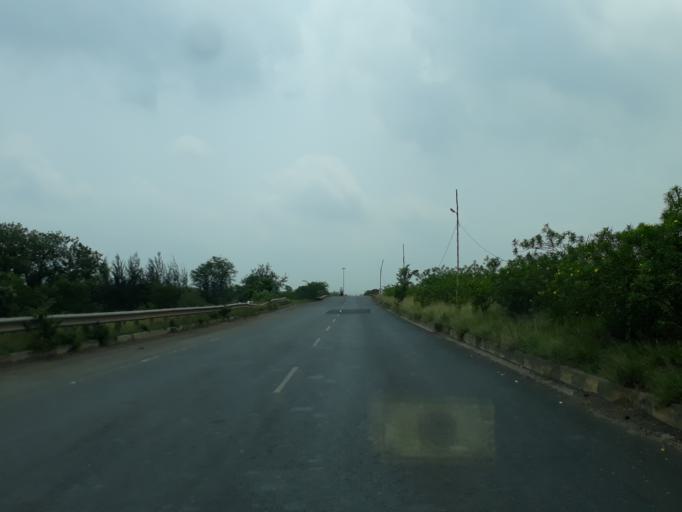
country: IN
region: West Bengal
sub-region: Purba Medinipur
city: Mahishadal
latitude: 22.1443
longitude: 87.9721
